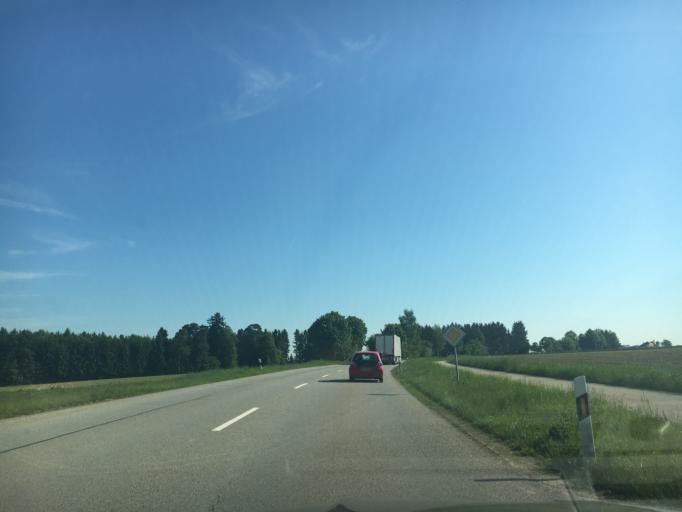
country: DE
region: Bavaria
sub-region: Upper Bavaria
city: Unterneukirchen
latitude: 48.1874
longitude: 12.6351
